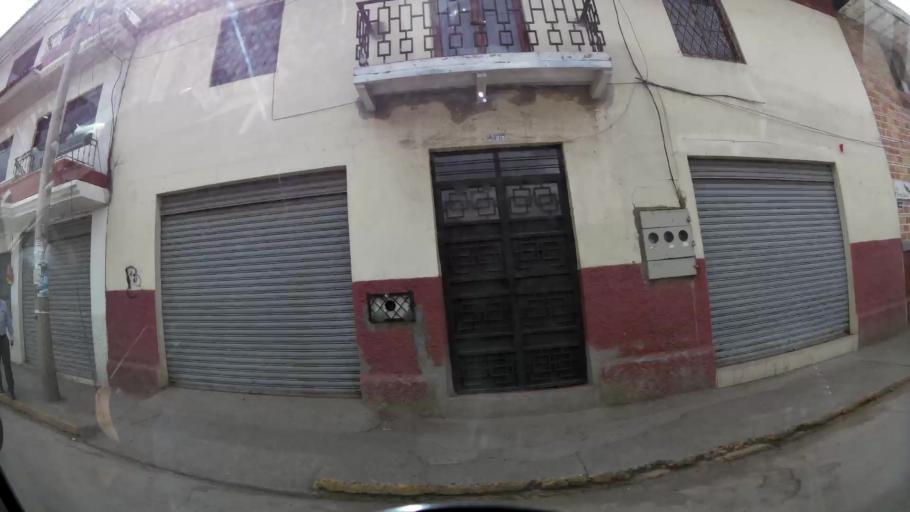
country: EC
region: Azuay
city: Cuenca
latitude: -2.8885
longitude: -78.9942
